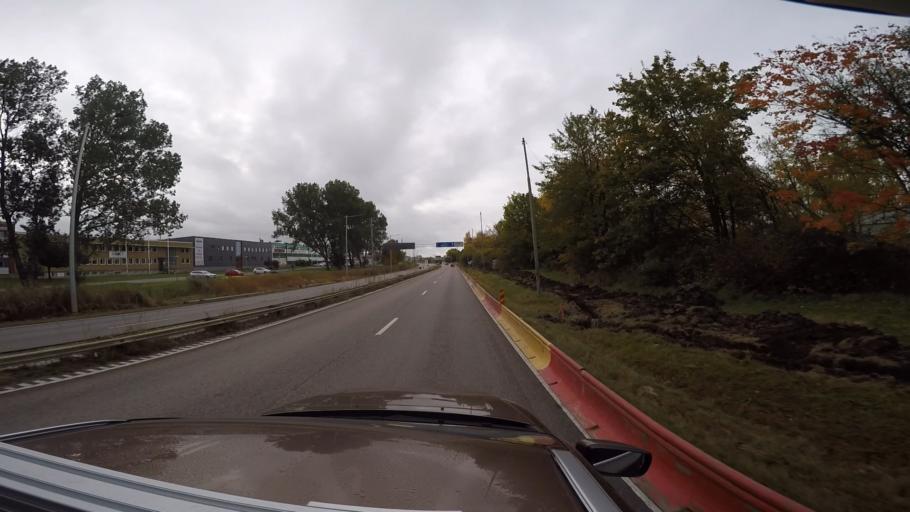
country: SE
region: Vaestra Goetaland
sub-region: Goteborg
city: Majorna
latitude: 57.6532
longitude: 11.9340
